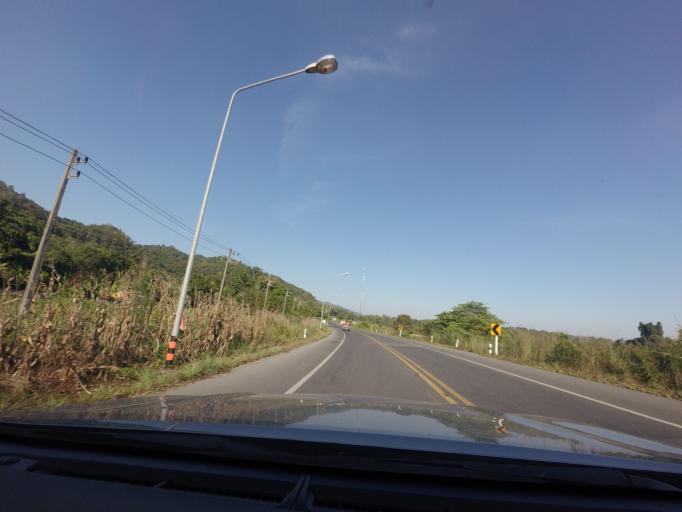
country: TH
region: Phrae
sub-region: Amphoe Wang Chin
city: Wang Chin
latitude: 17.9757
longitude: 99.6358
